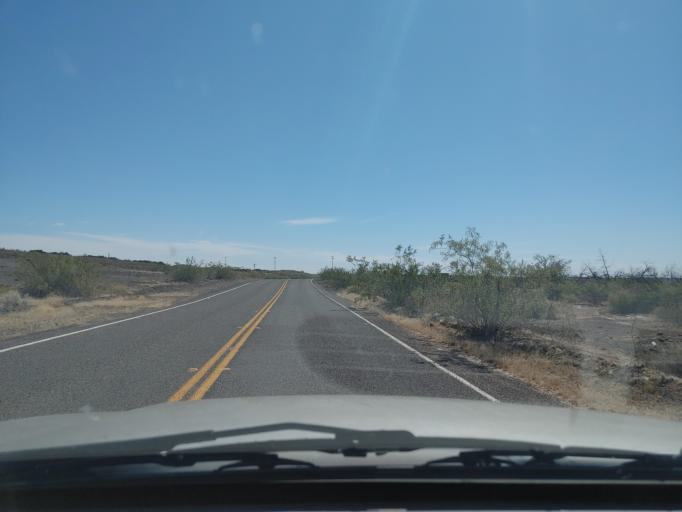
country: US
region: Arizona
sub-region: Maricopa County
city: Gila Bend
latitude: 32.9853
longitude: -113.3285
